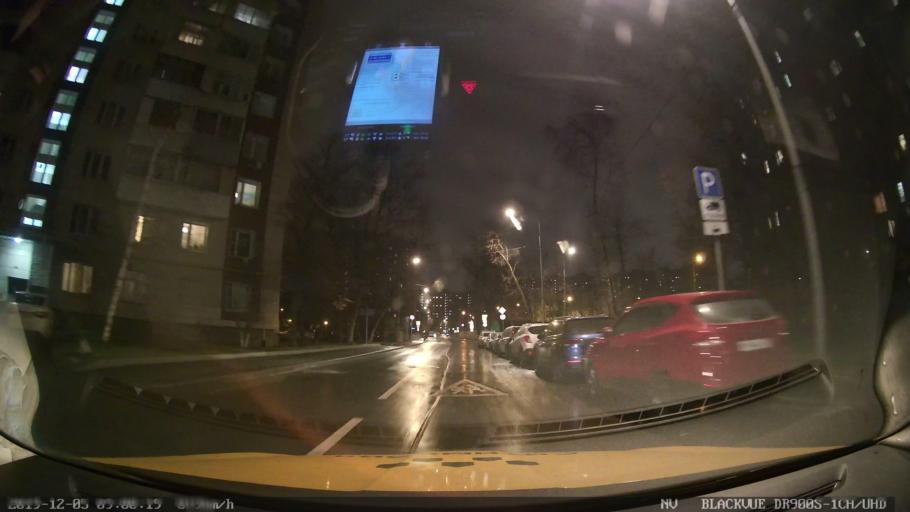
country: RU
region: Moskovskaya
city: Bogorodskoye
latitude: 55.8090
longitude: 37.7077
